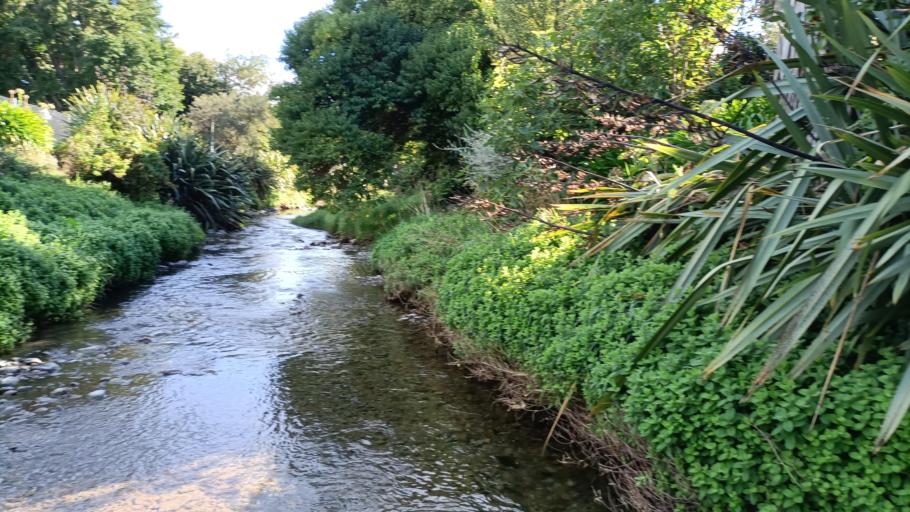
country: NZ
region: Nelson
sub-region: Nelson City
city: Nelson
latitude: -41.2797
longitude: 173.2889
